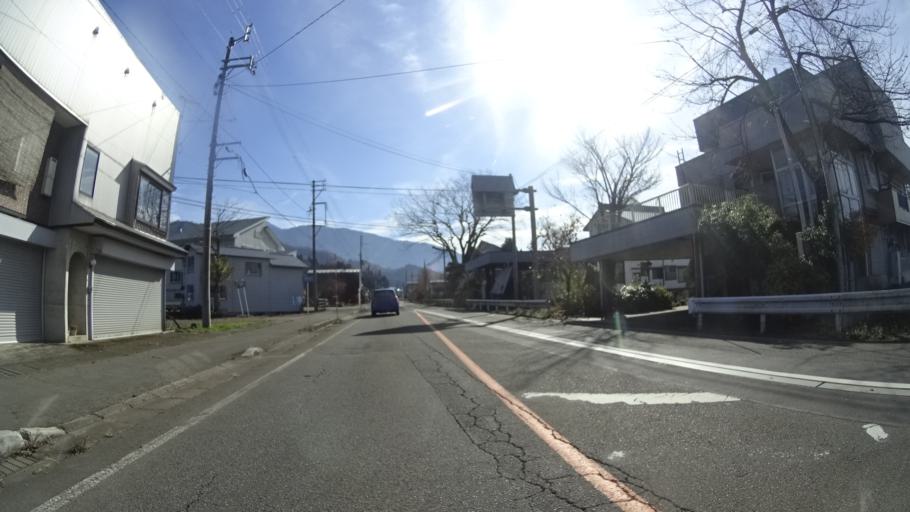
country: JP
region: Niigata
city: Muikamachi
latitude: 37.1738
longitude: 138.9676
